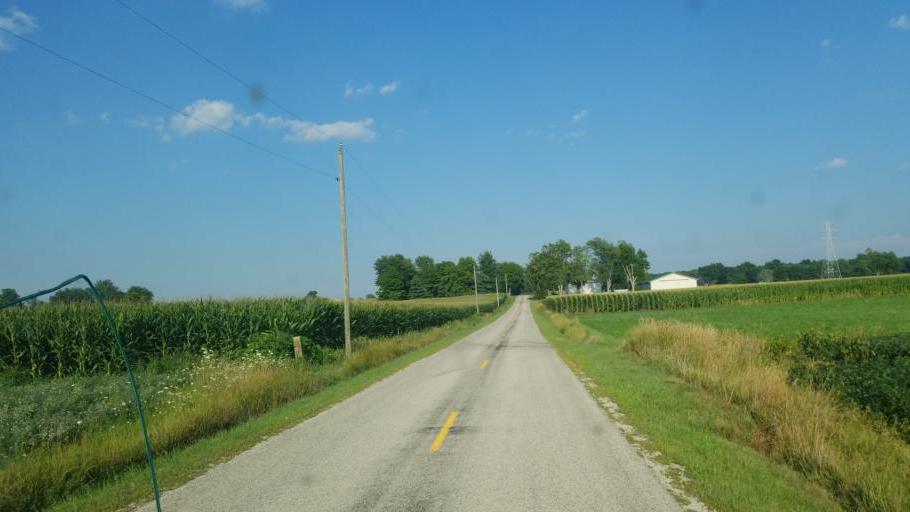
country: US
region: Ohio
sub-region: Crawford County
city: Bucyrus
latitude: 40.8545
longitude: -82.9215
